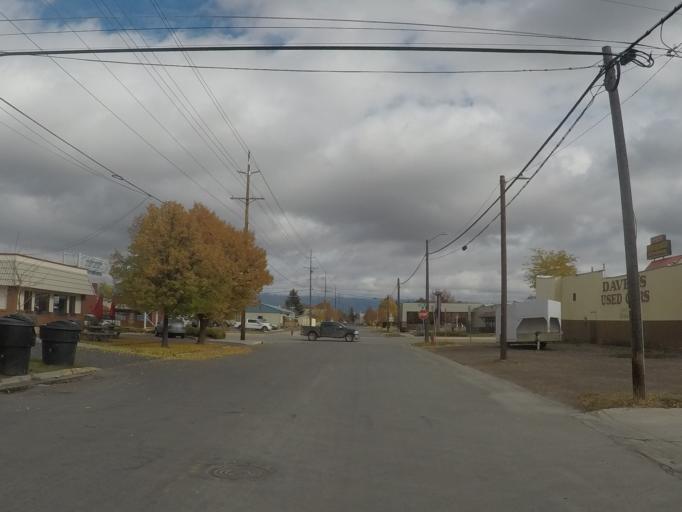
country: US
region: Montana
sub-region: Flathead County
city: Kalispell
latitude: 48.2011
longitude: -114.3161
